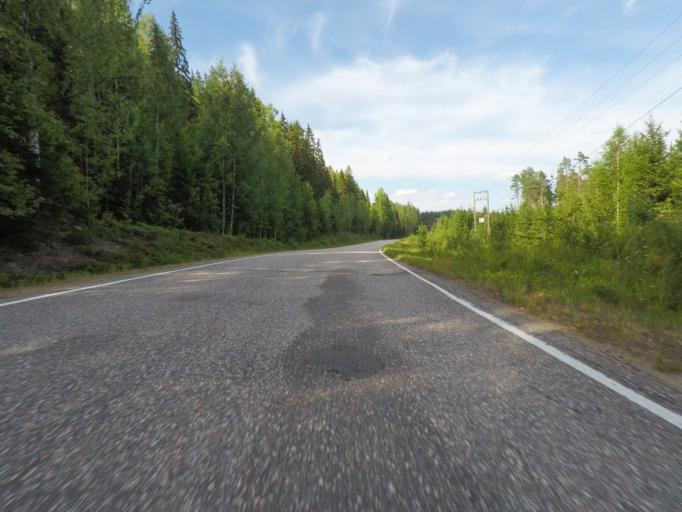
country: FI
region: Southern Savonia
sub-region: Savonlinna
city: Sulkava
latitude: 61.7263
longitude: 28.2047
